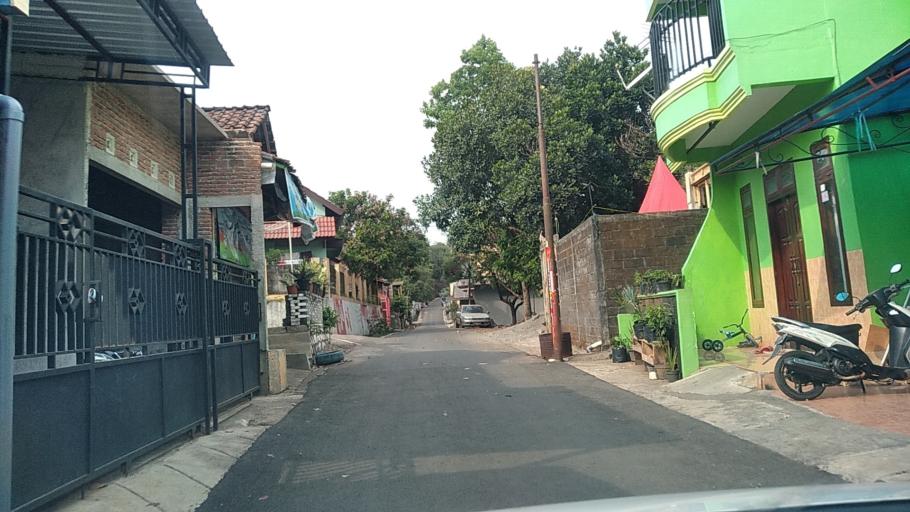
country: ID
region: Central Java
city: Ungaran
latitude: -7.1059
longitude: 110.3870
